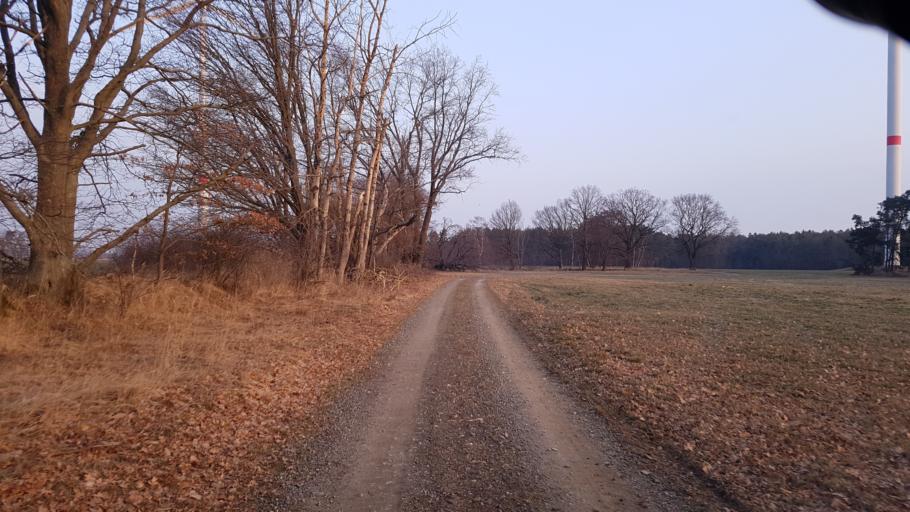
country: DE
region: Brandenburg
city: Falkenberg
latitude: 51.5730
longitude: 13.3076
